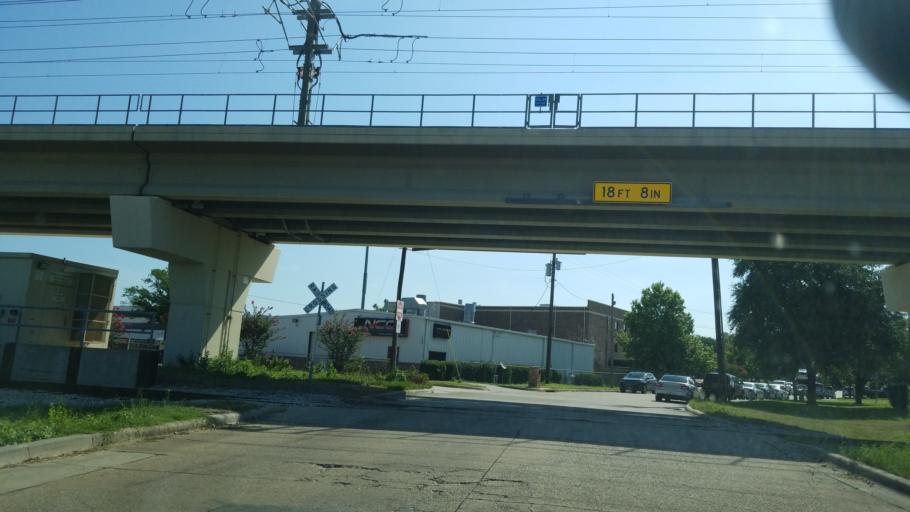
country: US
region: Texas
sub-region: Dallas County
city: Carrollton
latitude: 32.9637
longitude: -96.9149
